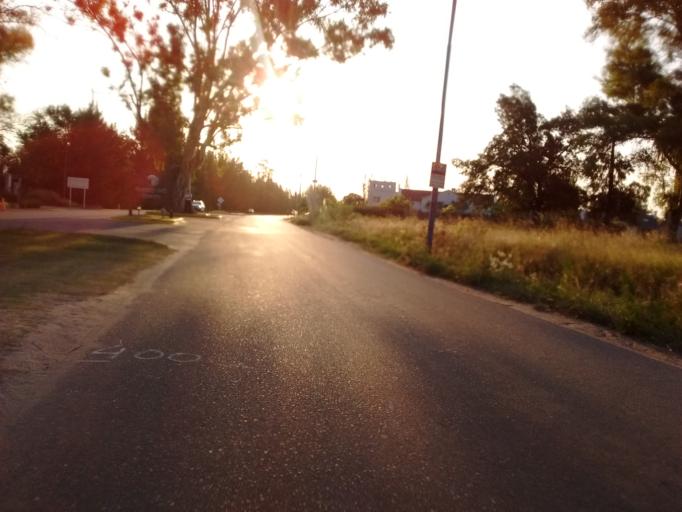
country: AR
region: Santa Fe
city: Funes
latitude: -32.9189
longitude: -60.7644
